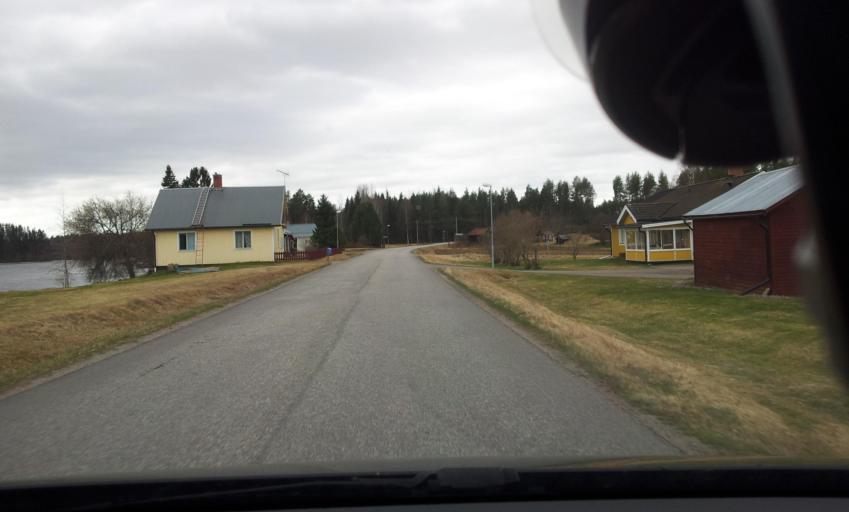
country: SE
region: Gaevleborg
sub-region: Ljusdals Kommun
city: Farila
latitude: 61.8079
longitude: 15.8990
